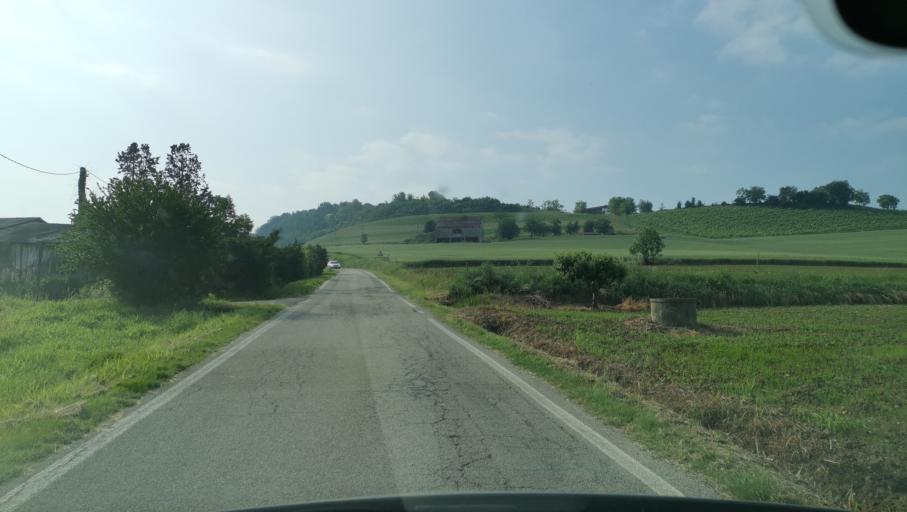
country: IT
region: Piedmont
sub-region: Provincia di Alessandria
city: Castelletto Merli
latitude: 45.0608
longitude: 8.2427
